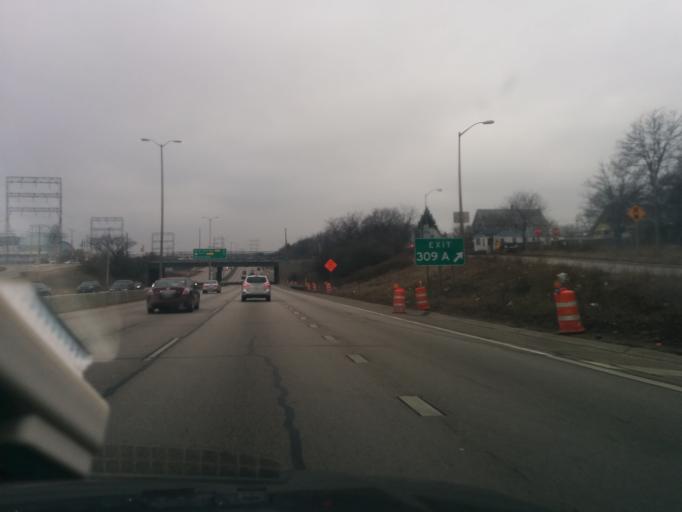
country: US
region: Wisconsin
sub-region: Milwaukee County
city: West Milwaukee
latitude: 43.0323
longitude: -87.9556
